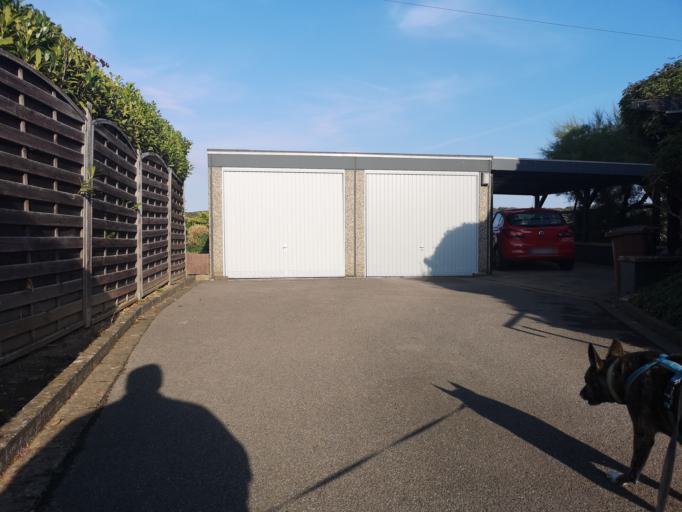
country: DE
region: North Rhine-Westphalia
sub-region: Regierungsbezirk Koln
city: Kreuzau
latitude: 50.7541
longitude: 6.4916
